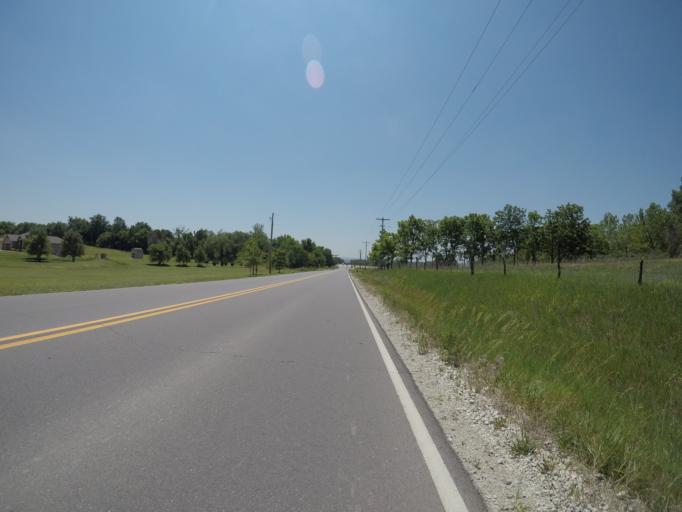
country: US
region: Kansas
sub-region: Riley County
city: Manhattan
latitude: 39.2043
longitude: -96.4403
